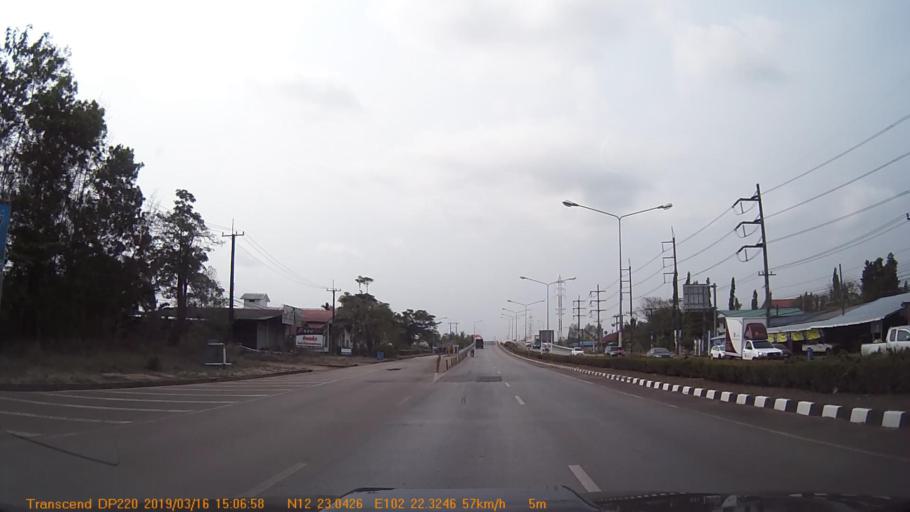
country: TH
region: Trat
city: Khao Saming
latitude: 12.3843
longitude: 102.3719
